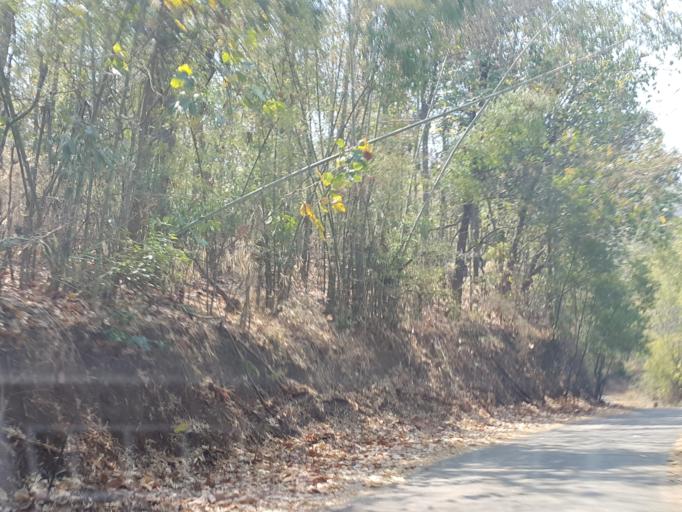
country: TH
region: Chiang Mai
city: Samoeng
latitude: 18.7999
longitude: 98.8100
